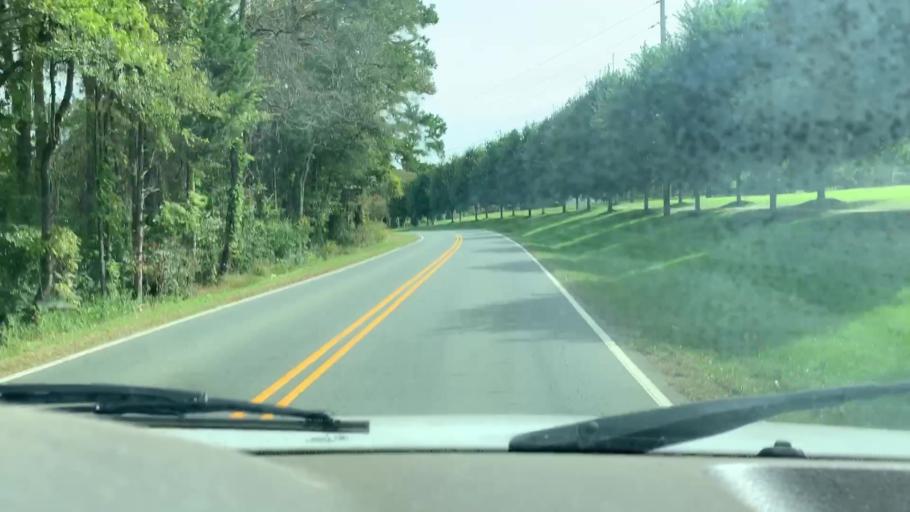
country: US
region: North Carolina
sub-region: Mecklenburg County
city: Huntersville
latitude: 35.4136
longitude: -80.8256
